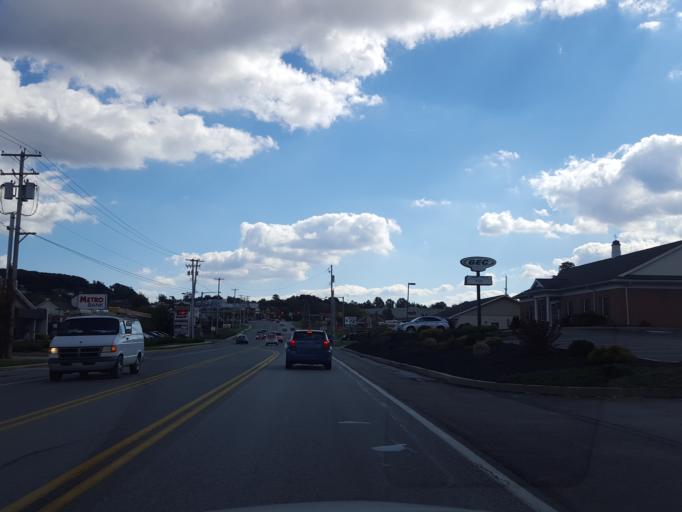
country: US
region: Pennsylvania
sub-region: York County
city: Yoe
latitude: 39.9198
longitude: -76.6324
